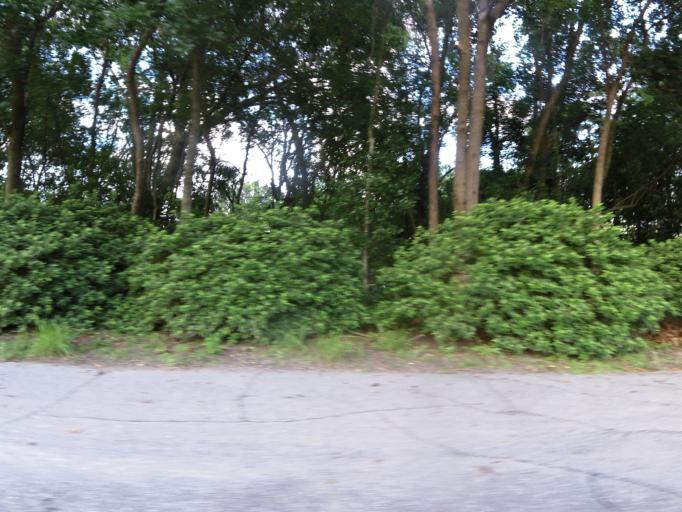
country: US
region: Florida
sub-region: Duval County
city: Jacksonville
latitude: 30.2957
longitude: -81.6198
